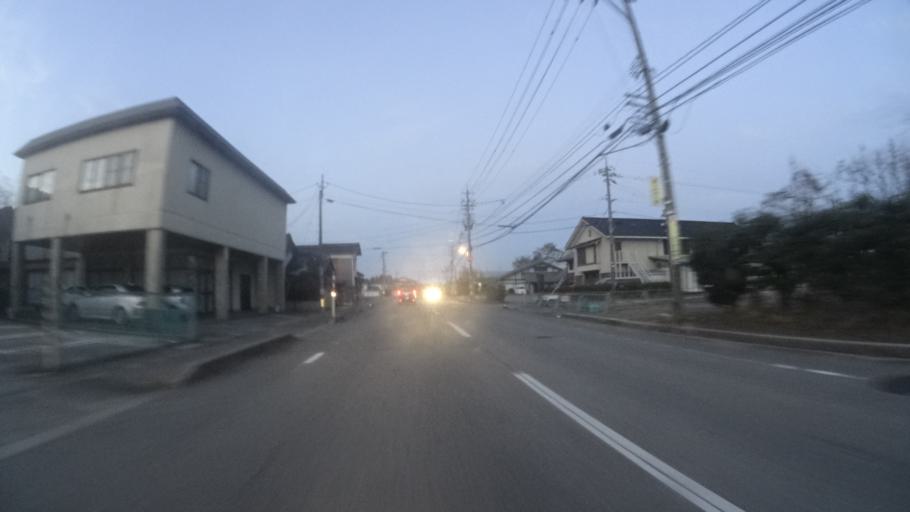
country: JP
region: Ishikawa
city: Nanao
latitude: 37.3815
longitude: 136.8867
